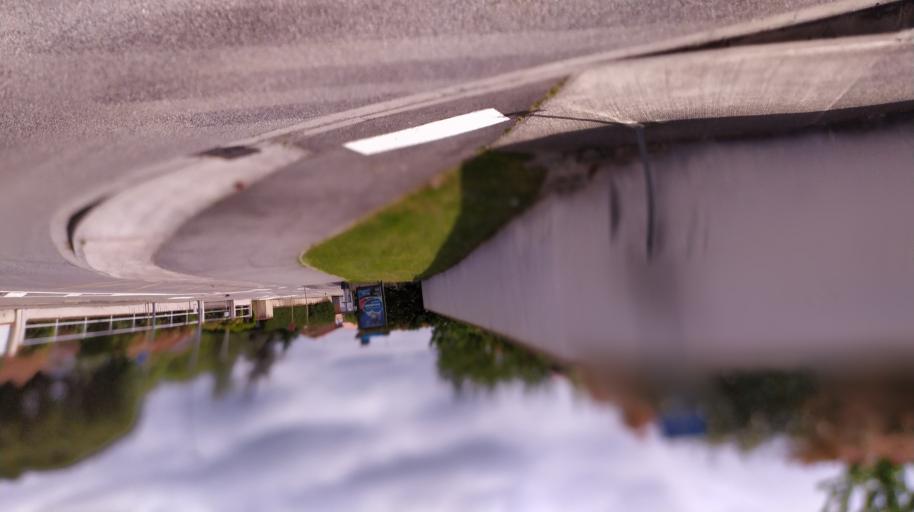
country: FR
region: Midi-Pyrenees
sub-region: Departement de la Haute-Garonne
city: Plaisance-du-Touch
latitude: 43.5814
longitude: 1.2973
